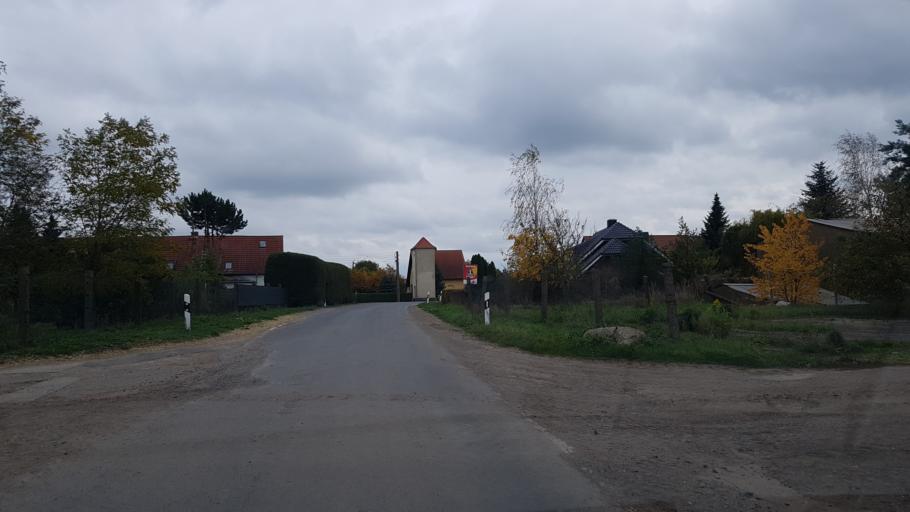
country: DE
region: Saxony
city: Dahlen
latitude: 51.3690
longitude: 12.9872
